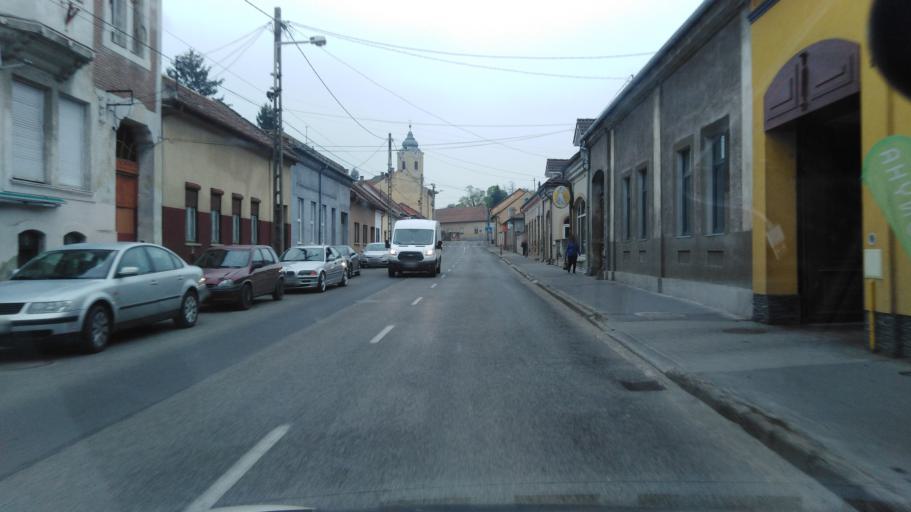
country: HU
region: Nograd
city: Balassagyarmat
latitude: 48.0778
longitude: 19.2951
